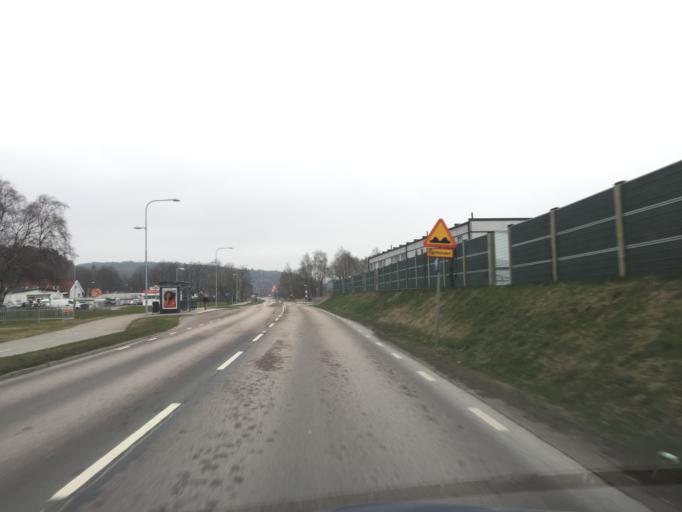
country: SE
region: Vaestra Goetaland
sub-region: Partille Kommun
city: Partille
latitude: 57.7391
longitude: 12.0683
